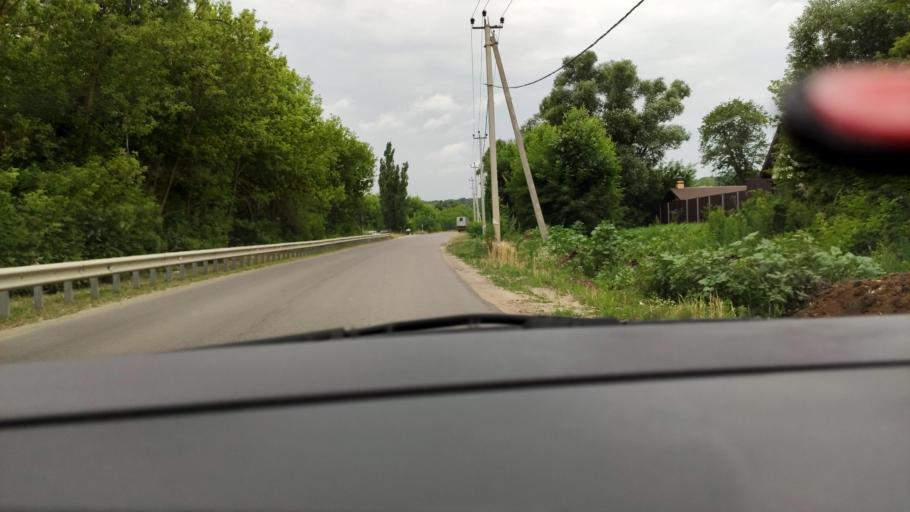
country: RU
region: Voronezj
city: Ramon'
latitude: 51.9051
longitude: 39.3491
